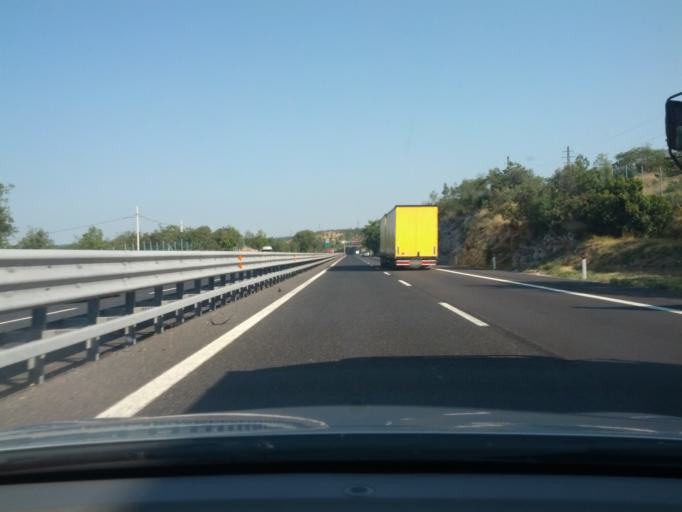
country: IT
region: Friuli Venezia Giulia
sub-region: Provincia di Trieste
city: Duino
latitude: 45.7848
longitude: 13.5963
